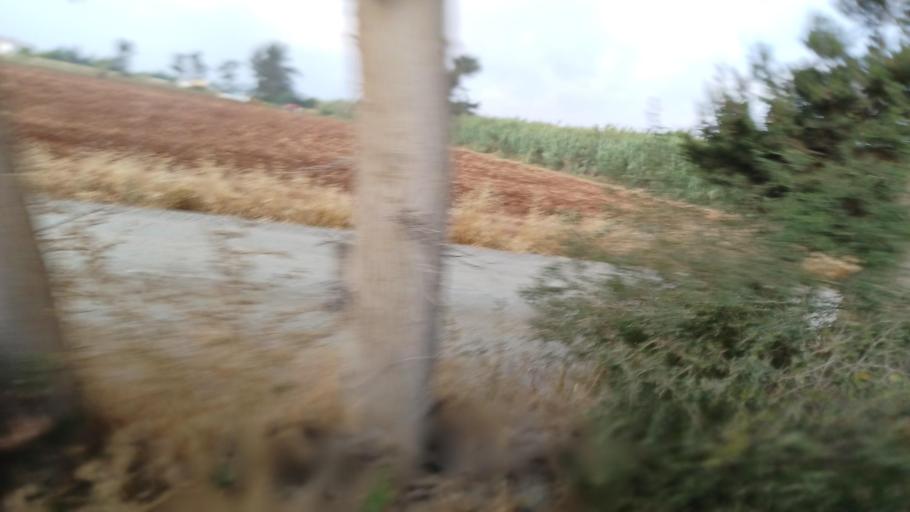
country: CY
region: Larnaka
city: Meneou
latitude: 34.8453
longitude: 33.5973
